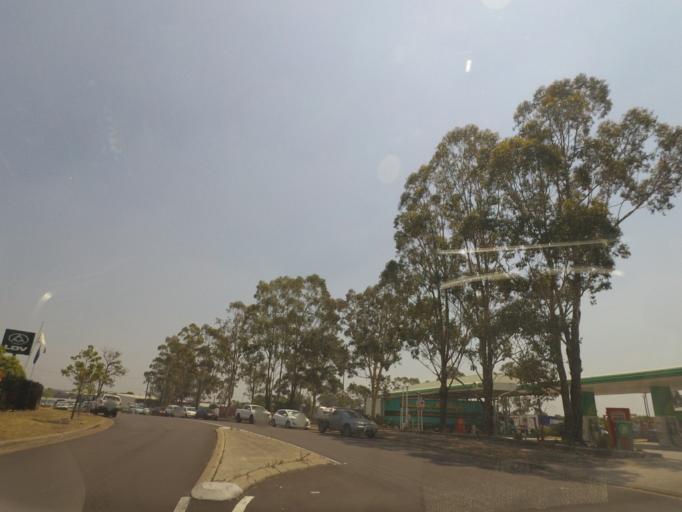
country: AU
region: New South Wales
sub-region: Newcastle
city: Beresfield
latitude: -32.8119
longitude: 151.6391
